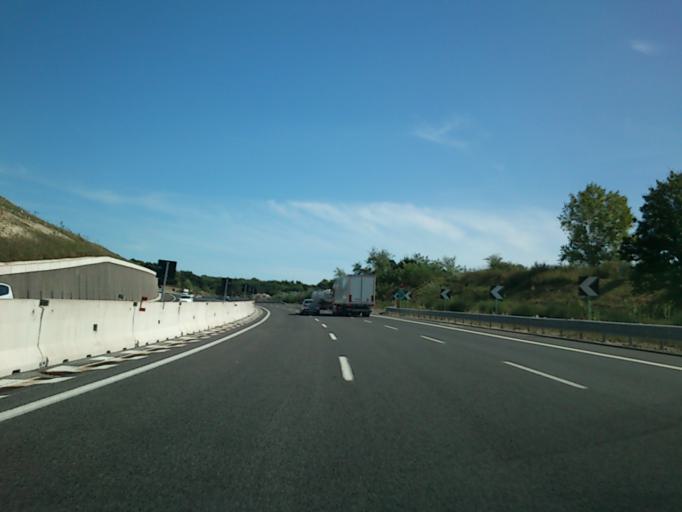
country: IT
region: The Marches
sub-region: Provincia di Pesaro e Urbino
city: Pesaro
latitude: 43.8808
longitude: 12.9066
